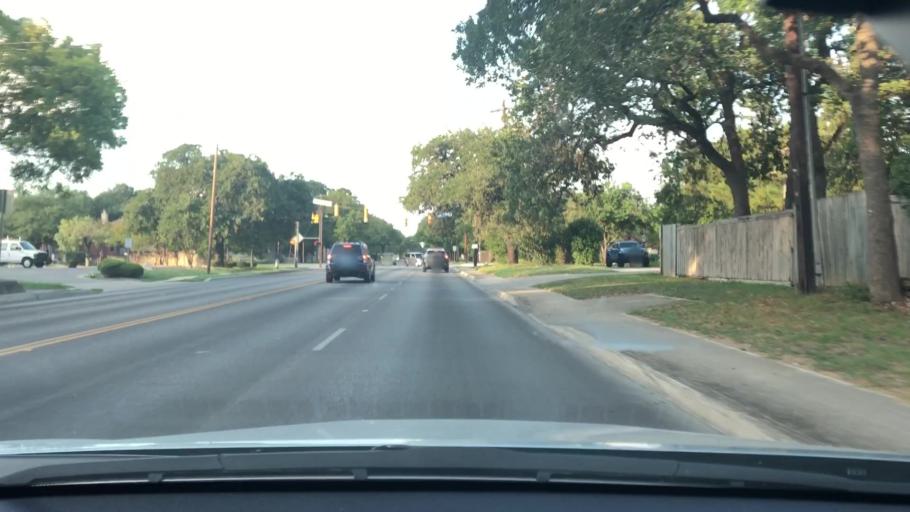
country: US
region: Texas
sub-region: Bexar County
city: Hollywood Park
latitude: 29.5695
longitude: -98.4507
